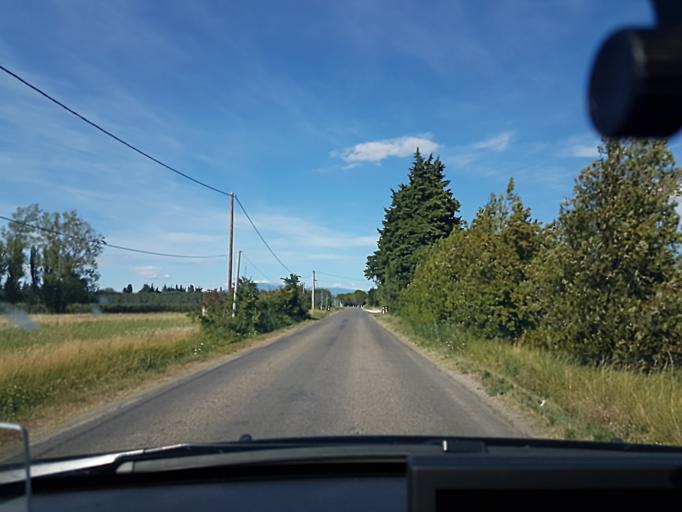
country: FR
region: Provence-Alpes-Cote d'Azur
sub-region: Departement du Vaucluse
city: Caumont-sur-Durance
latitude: 43.9111
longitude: 4.9670
